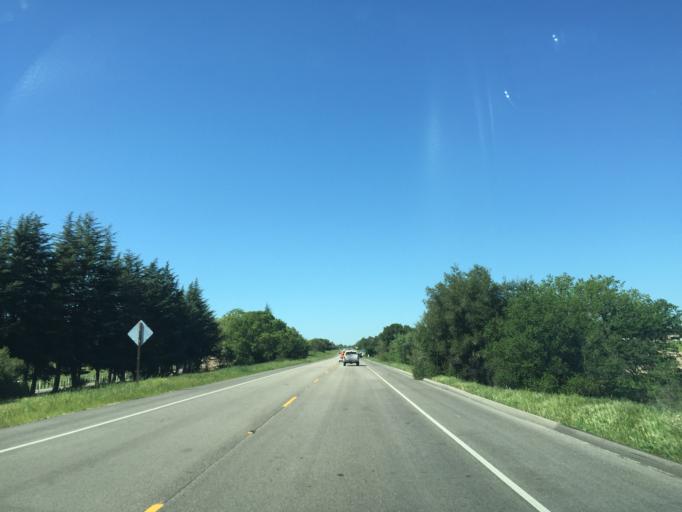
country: US
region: California
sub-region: Santa Barbara County
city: Santa Ynez
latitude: 34.6436
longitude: -120.0894
